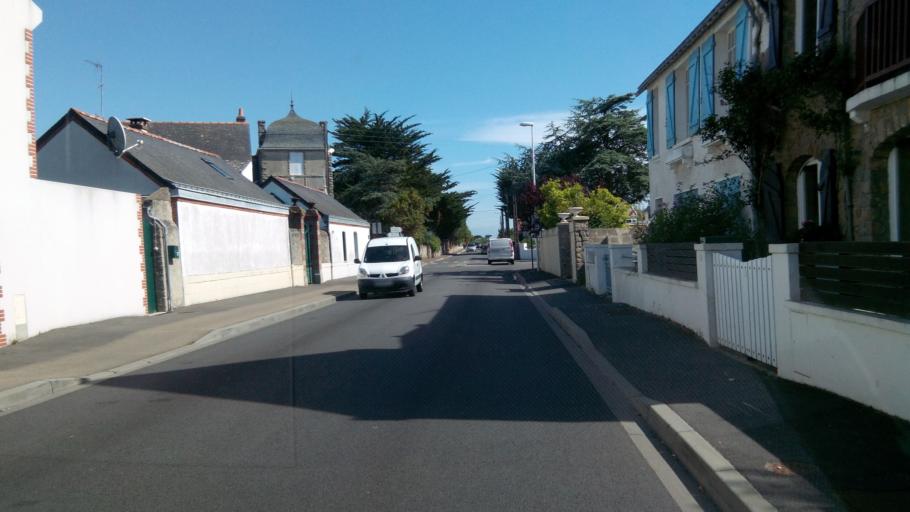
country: FR
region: Pays de la Loire
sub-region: Departement de la Loire-Atlantique
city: Le Croisic
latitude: 47.2884
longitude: -2.5103
